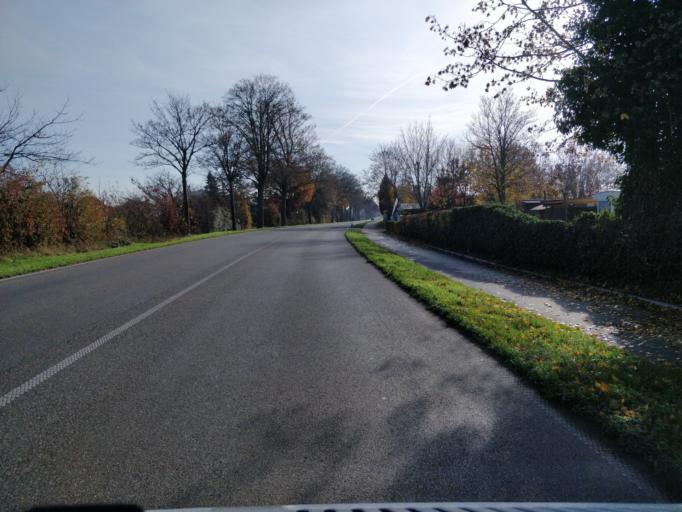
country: DE
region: North Rhine-Westphalia
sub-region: Regierungsbezirk Dusseldorf
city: Mehrhoog
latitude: 51.7553
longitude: 6.4838
